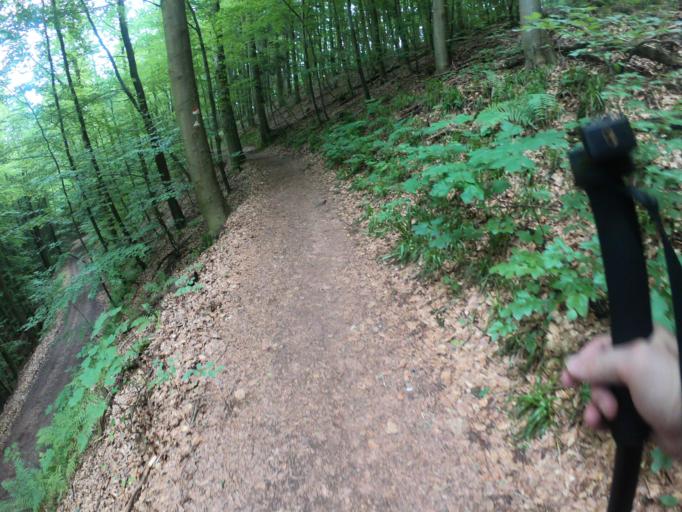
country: DE
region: Rheinland-Pfalz
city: Annweiler am Trifels
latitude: 49.1995
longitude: 7.9799
